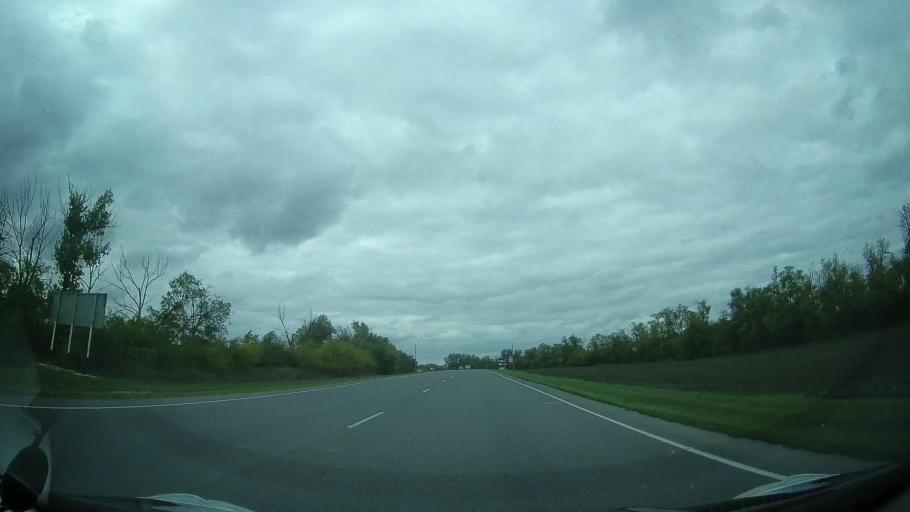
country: RU
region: Rostov
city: Mechetinskaya
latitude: 46.7505
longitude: 40.4619
